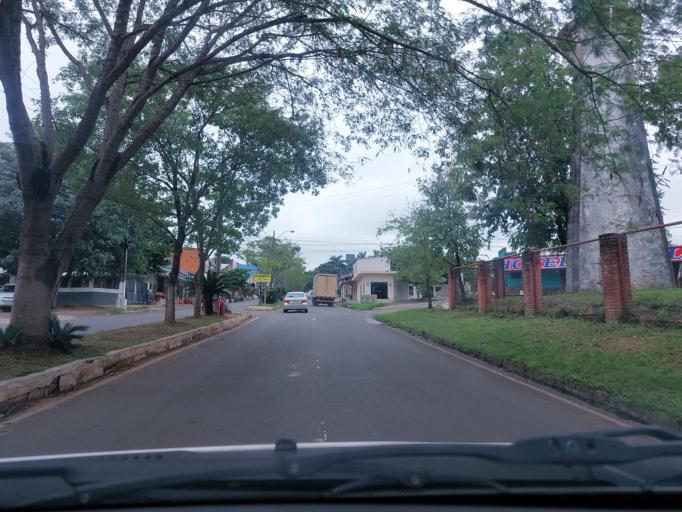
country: PY
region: San Pedro
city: Guayaybi
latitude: -24.6645
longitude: -56.4371
